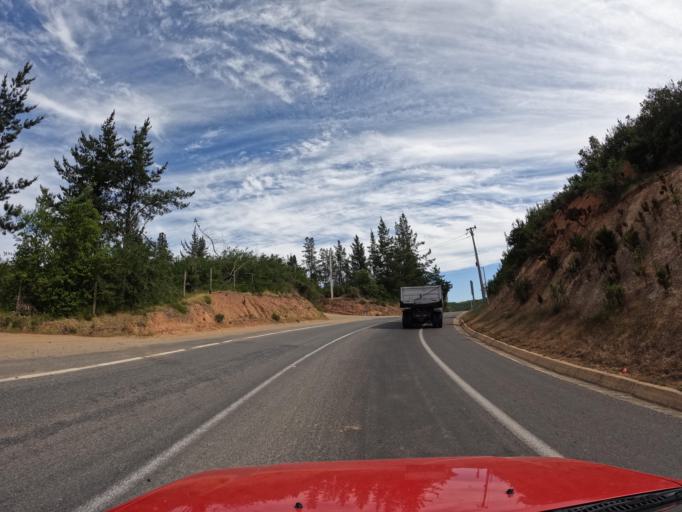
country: CL
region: Maule
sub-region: Provincia de Talca
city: Talca
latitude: -35.1663
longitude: -71.9728
